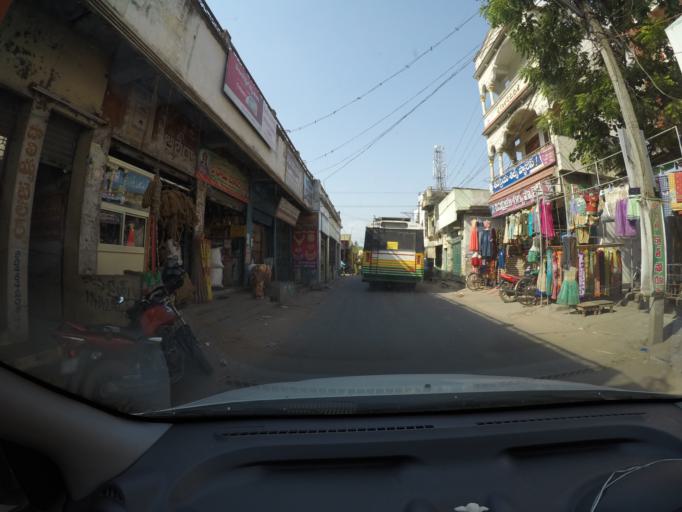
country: IN
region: Andhra Pradesh
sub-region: Krishna
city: Kankipadu
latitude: 16.4350
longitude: 80.7683
